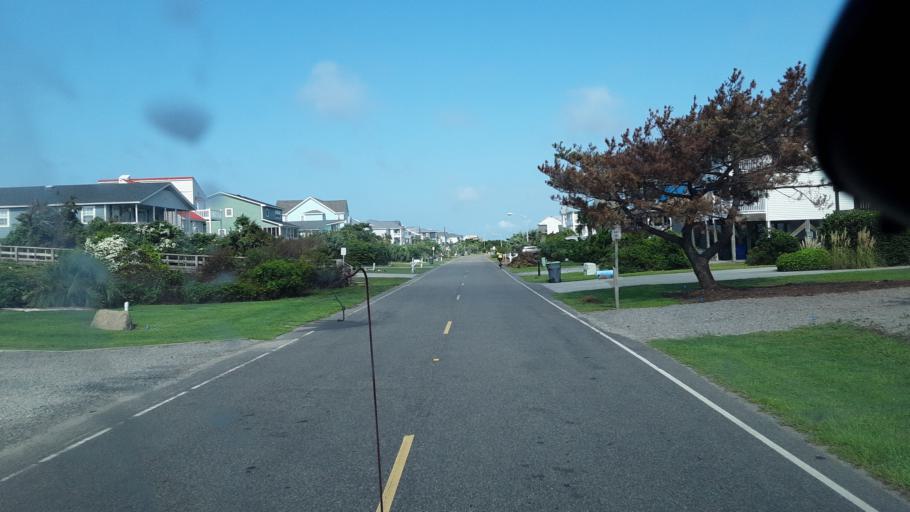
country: US
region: North Carolina
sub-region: Brunswick County
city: Southport
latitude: 33.8940
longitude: -78.0408
